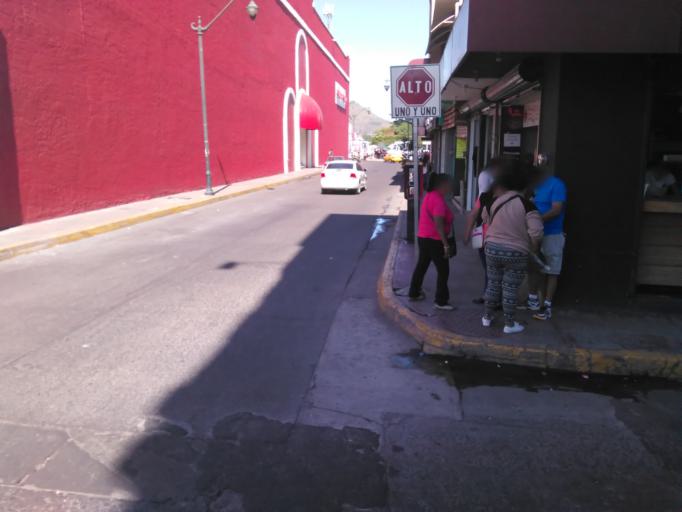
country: MX
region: Nayarit
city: Tepic
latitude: 21.5098
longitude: -104.8915
